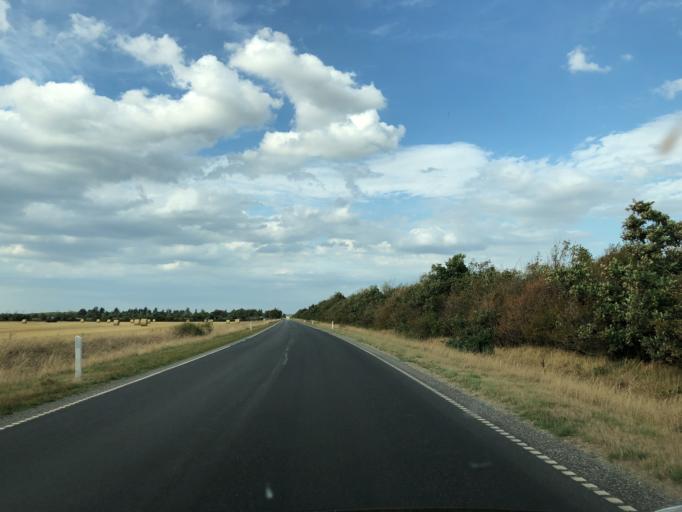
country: DK
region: Central Jutland
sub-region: Holstebro Kommune
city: Ulfborg
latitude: 56.3783
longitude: 8.4476
